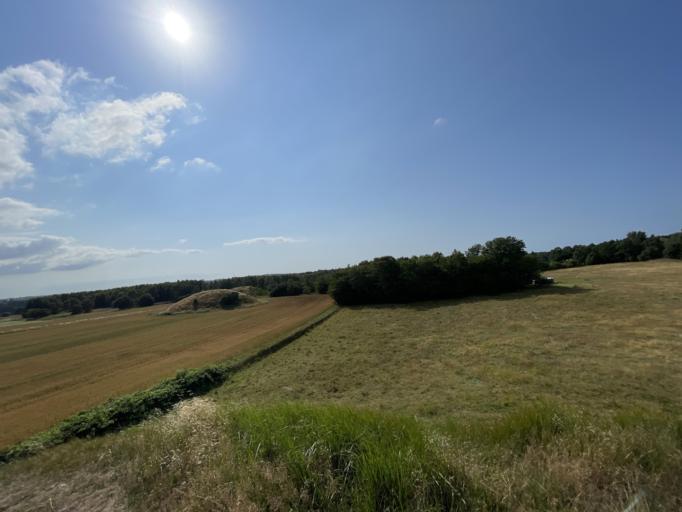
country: DK
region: Capital Region
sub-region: Gribskov Kommune
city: Helsinge
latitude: 56.0901
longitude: 12.1822
